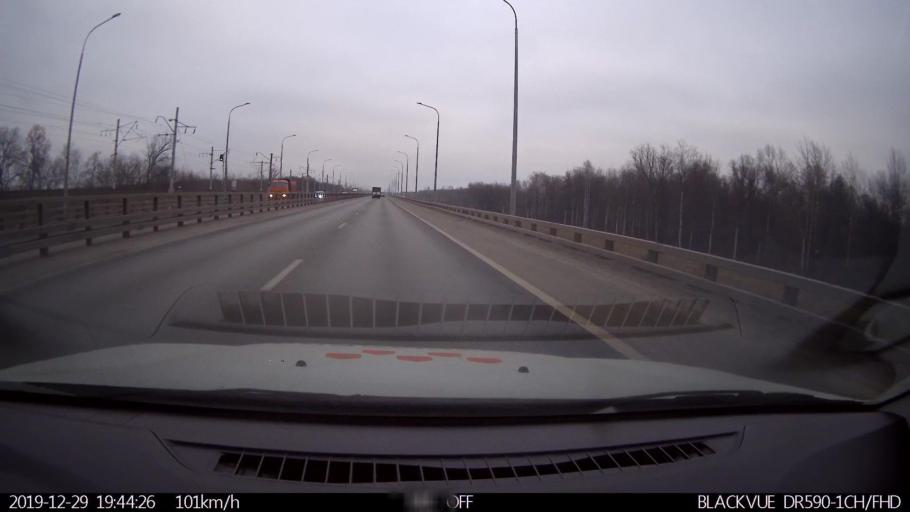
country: RU
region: Nizjnij Novgorod
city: Neklyudovo
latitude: 56.3748
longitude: 43.9510
